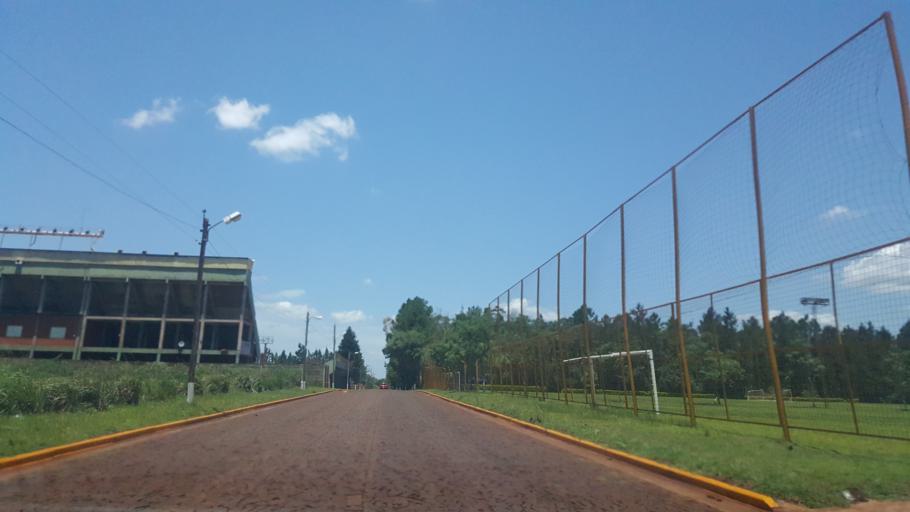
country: AR
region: Misiones
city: Garupa
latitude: -27.4984
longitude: -55.8538
